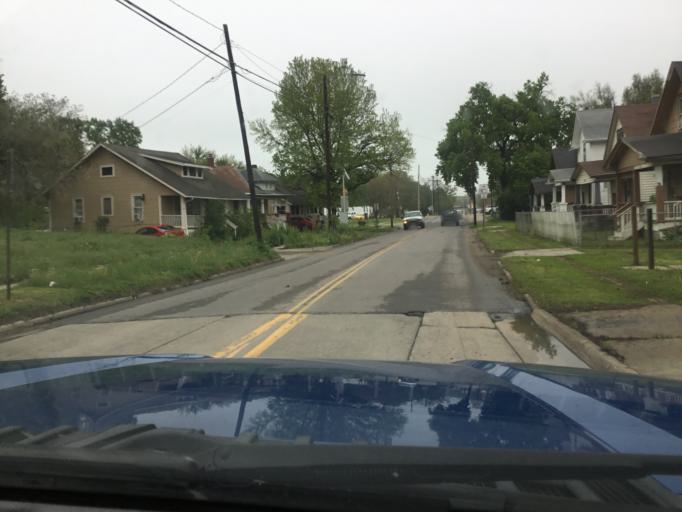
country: US
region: Kansas
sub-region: Shawnee County
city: Topeka
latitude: 39.0369
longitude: -95.6775
